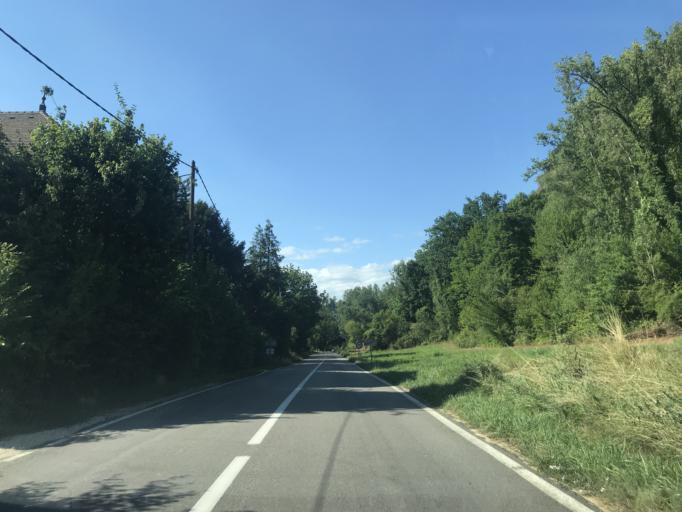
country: FR
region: Rhone-Alpes
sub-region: Departement de la Savoie
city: Yenne
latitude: 45.7546
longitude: 5.7865
